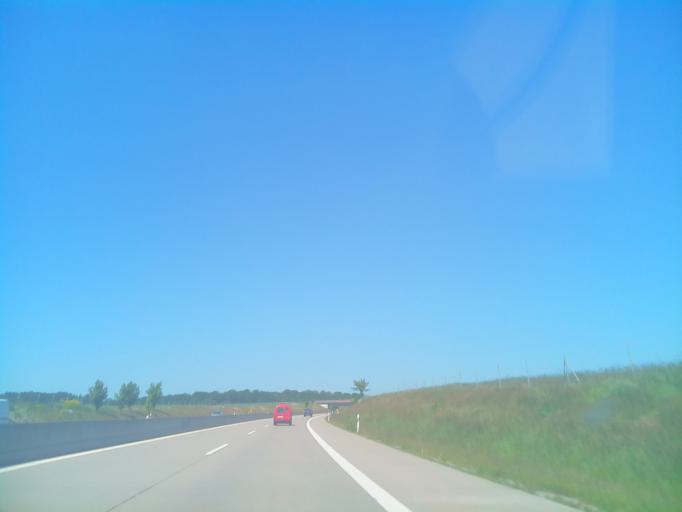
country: DE
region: Bavaria
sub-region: Regierungsbezirk Unterfranken
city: Strahlungen
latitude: 50.2879
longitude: 10.2625
